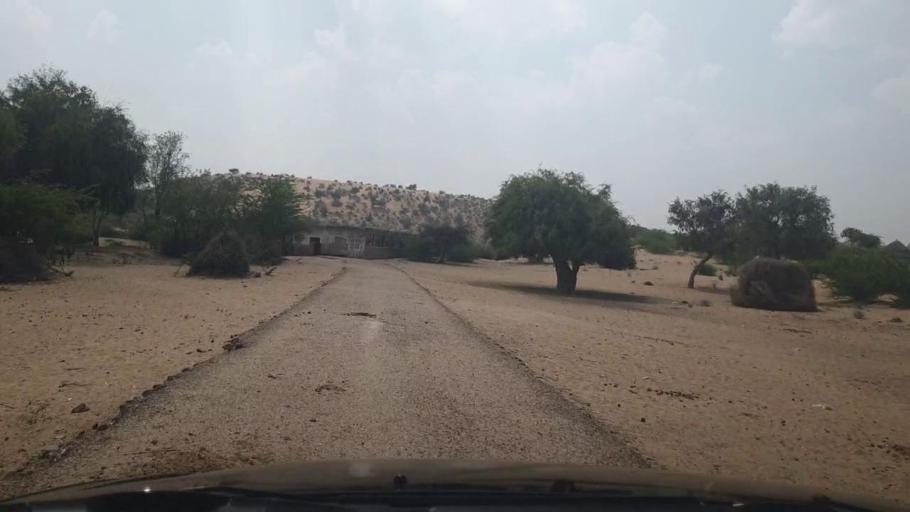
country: PK
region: Sindh
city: Islamkot
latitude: 24.9903
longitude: 70.4931
